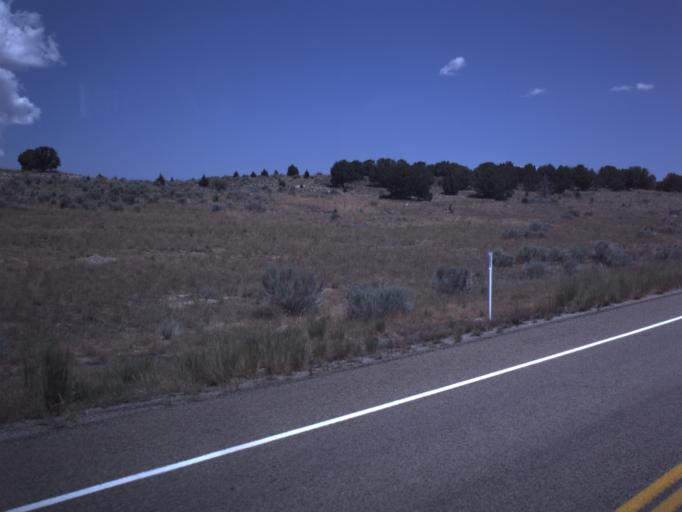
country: US
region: Utah
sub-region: Juab County
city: Nephi
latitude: 39.6624
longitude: -112.0601
